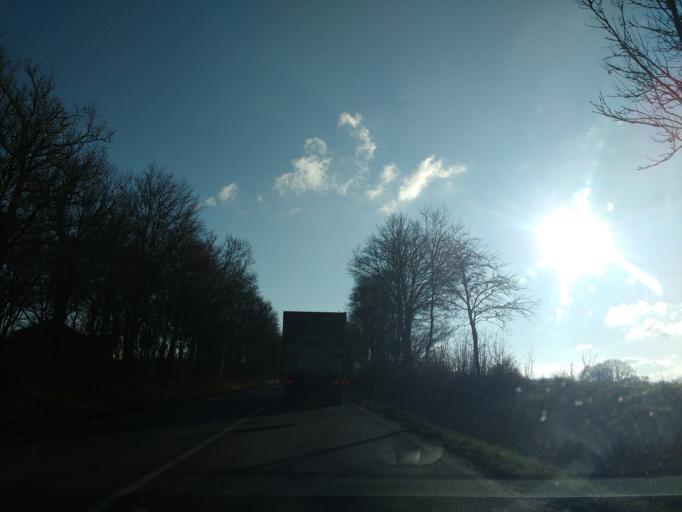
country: DE
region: Hesse
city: Schwalmstadt
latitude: 50.9037
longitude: 9.2649
